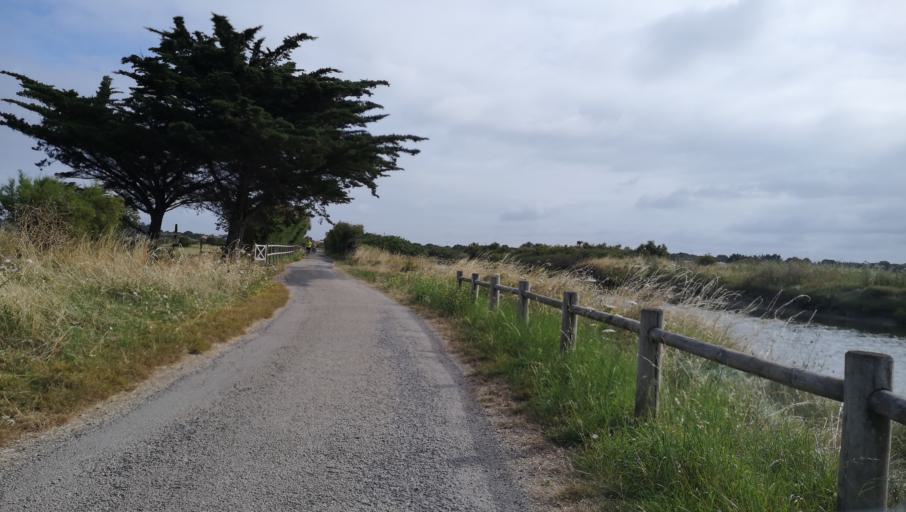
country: FR
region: Pays de la Loire
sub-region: Departement de la Vendee
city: Olonne-sur-Mer
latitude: 46.5362
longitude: -1.8049
